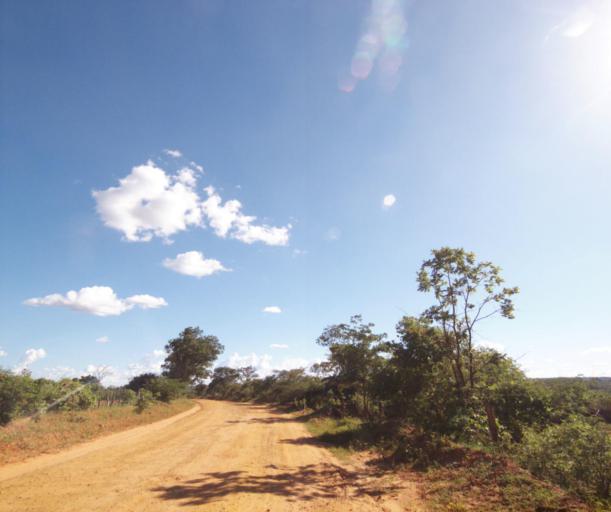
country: BR
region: Bahia
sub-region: Carinhanha
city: Carinhanha
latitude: -14.1930
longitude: -44.5470
